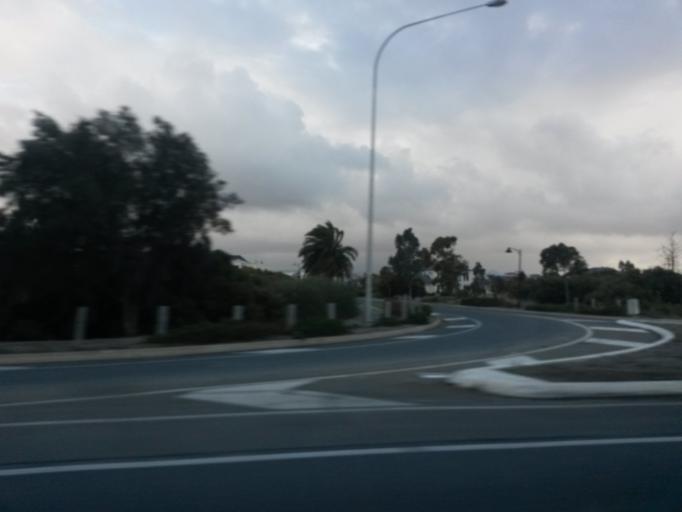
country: AU
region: South Australia
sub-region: Salisbury
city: Ingle Farm
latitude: -34.8072
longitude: 138.6014
